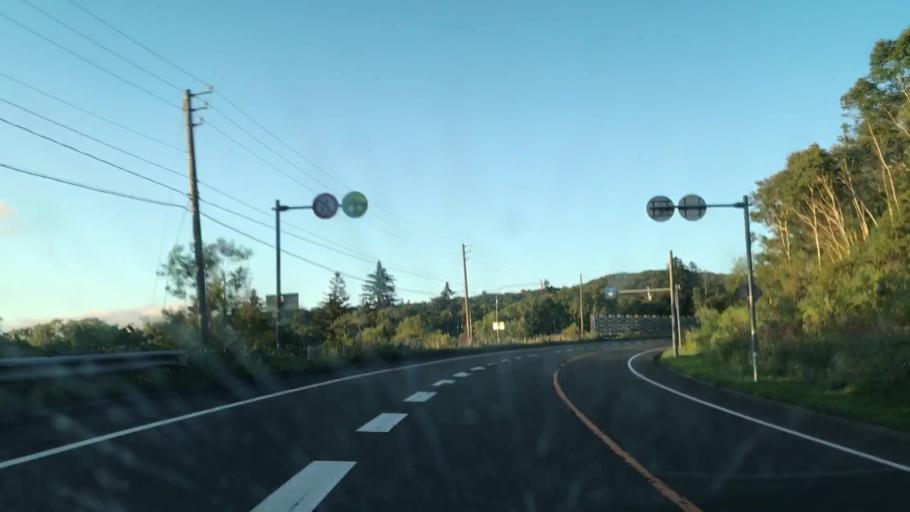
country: JP
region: Hokkaido
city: Sapporo
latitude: 42.8536
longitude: 141.0918
